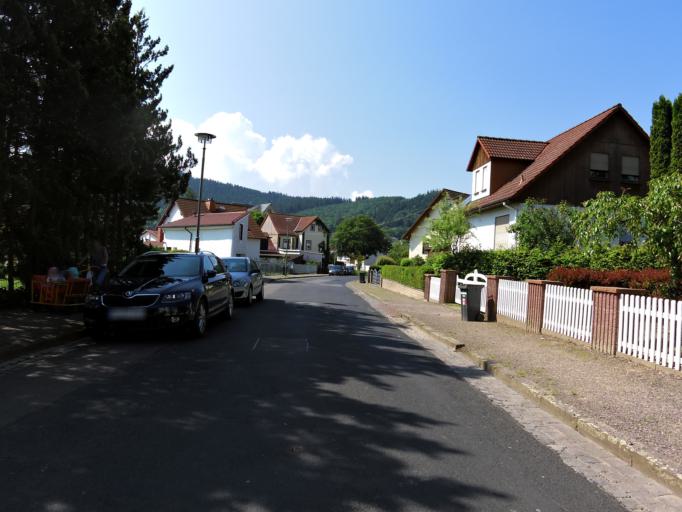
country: DE
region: Thuringia
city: Friedrichroda
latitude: 50.8605
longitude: 10.5697
